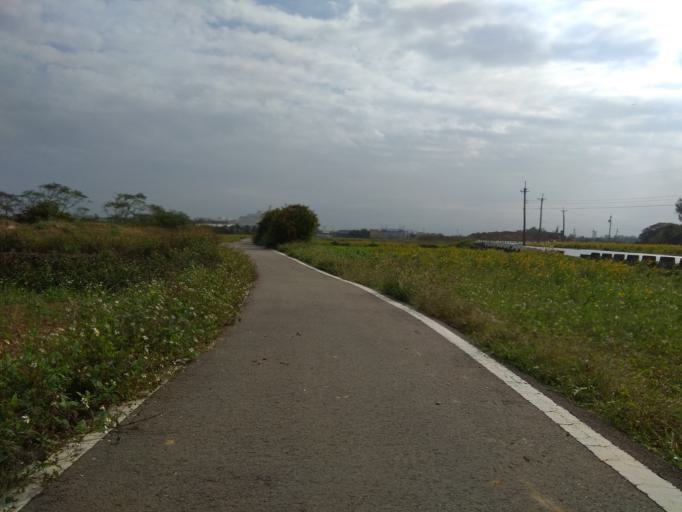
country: TW
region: Taiwan
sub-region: Hsinchu
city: Zhubei
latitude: 24.9806
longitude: 121.0322
